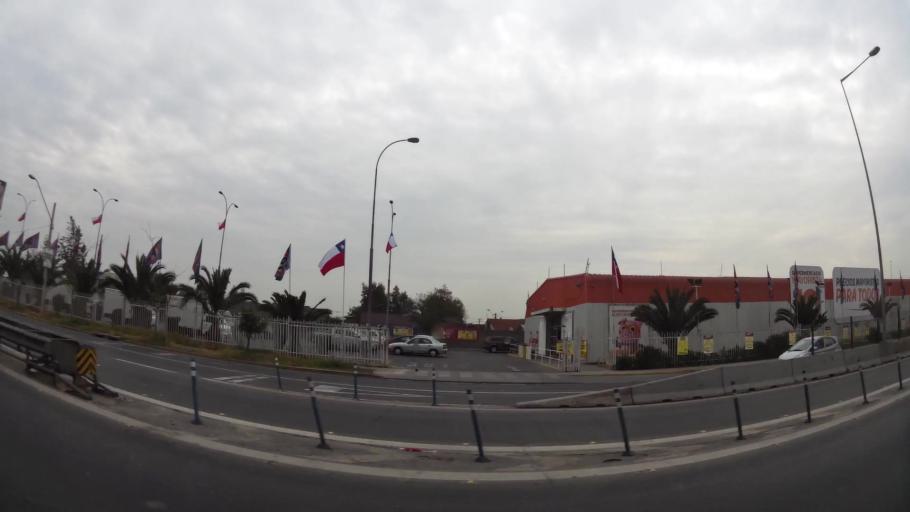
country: CL
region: Santiago Metropolitan
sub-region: Provincia de Santiago
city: Lo Prado
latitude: -33.5079
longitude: -70.7255
